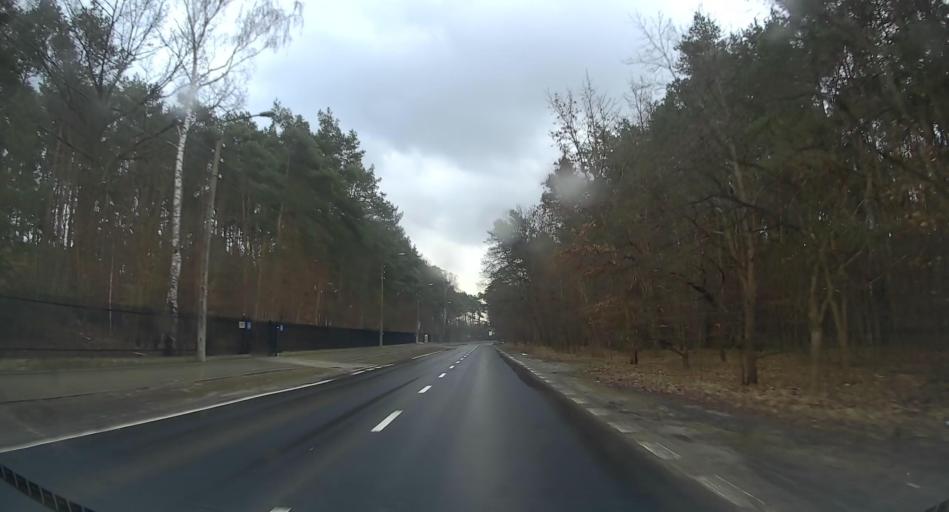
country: PL
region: Masovian Voivodeship
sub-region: Warszawa
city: Wawer
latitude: 52.1785
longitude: 21.1508
